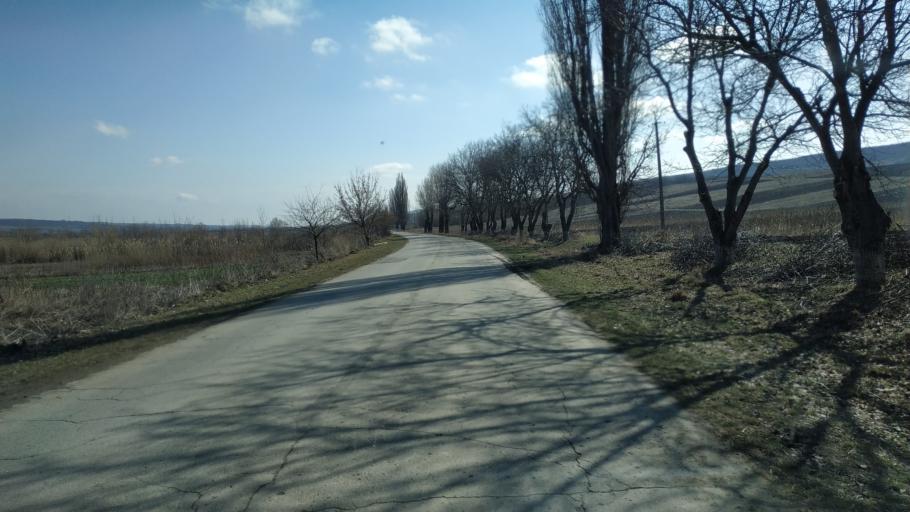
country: MD
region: Hincesti
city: Hincesti
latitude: 46.9487
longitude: 28.6161
